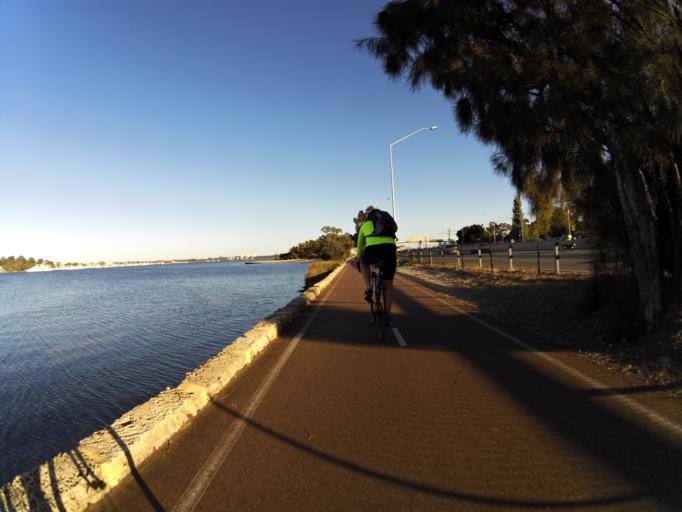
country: AU
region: Western Australia
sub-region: South Perth
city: Manning
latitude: -32.0060
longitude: 115.8541
